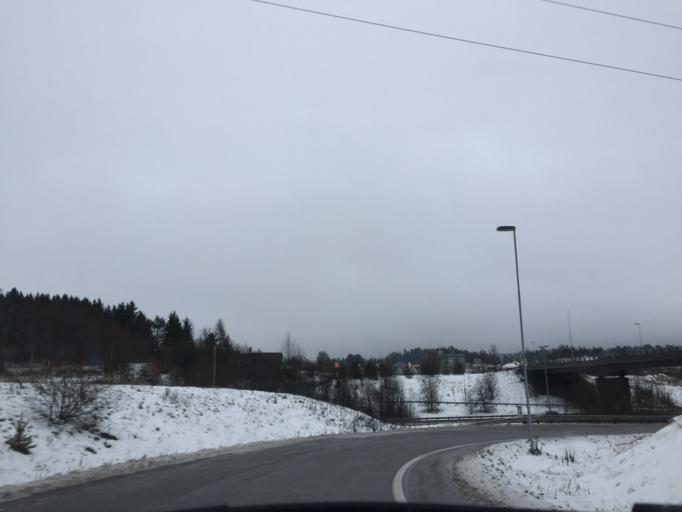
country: NO
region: Akershus
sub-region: Vestby
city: Vestby
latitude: 59.6029
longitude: 10.7361
